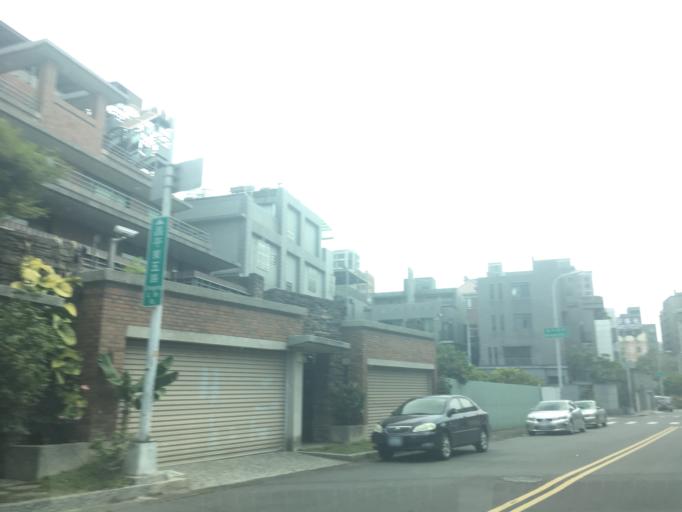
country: TW
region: Taiwan
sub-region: Taichung City
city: Taichung
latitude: 24.1916
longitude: 120.6885
